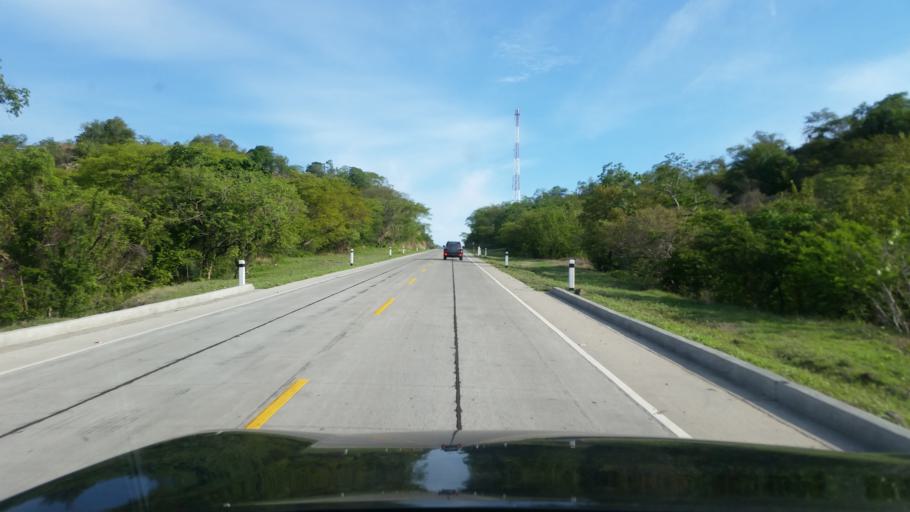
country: NI
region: Leon
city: Nagarote
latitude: 12.1683
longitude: -86.6628
